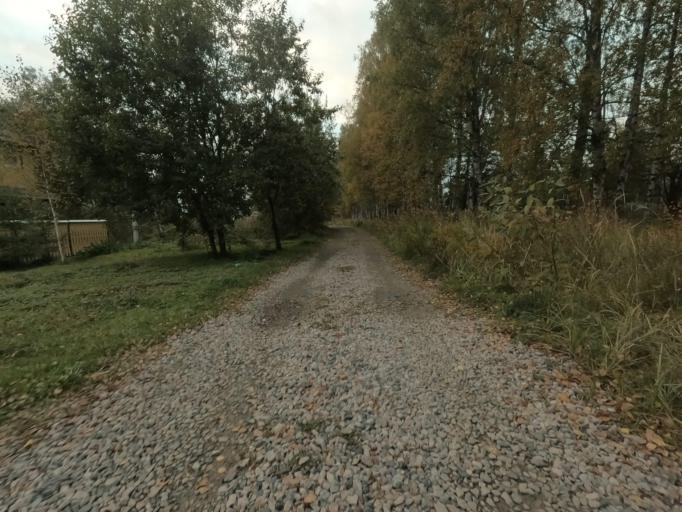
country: RU
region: Leningrad
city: Pavlovo
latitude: 59.8110
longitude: 30.9239
